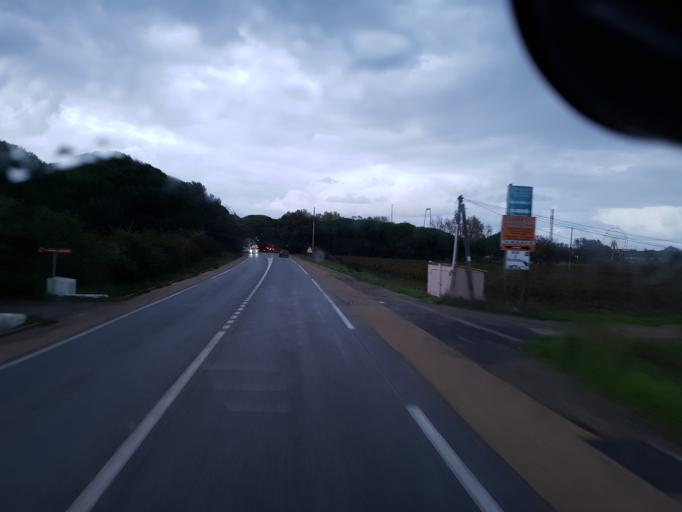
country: FR
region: Provence-Alpes-Cote d'Azur
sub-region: Departement du Var
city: Gassin
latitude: 43.2571
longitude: 6.5750
